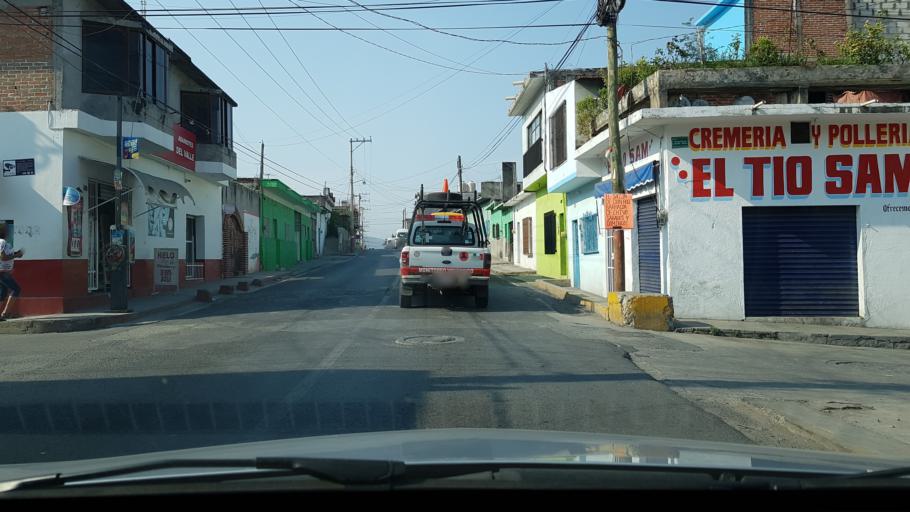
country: MX
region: Morelos
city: Tlaquiltenango
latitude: 18.6355
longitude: -99.1616
